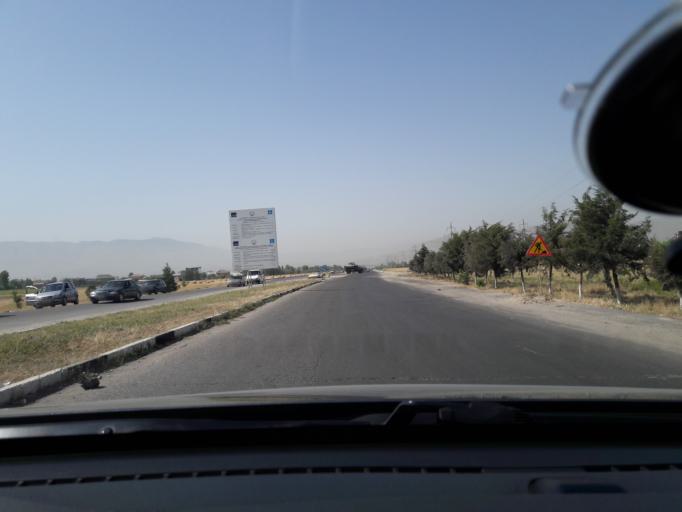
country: TJ
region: Dushanbe
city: Dushanbe
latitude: 38.4981
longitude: 68.7550
